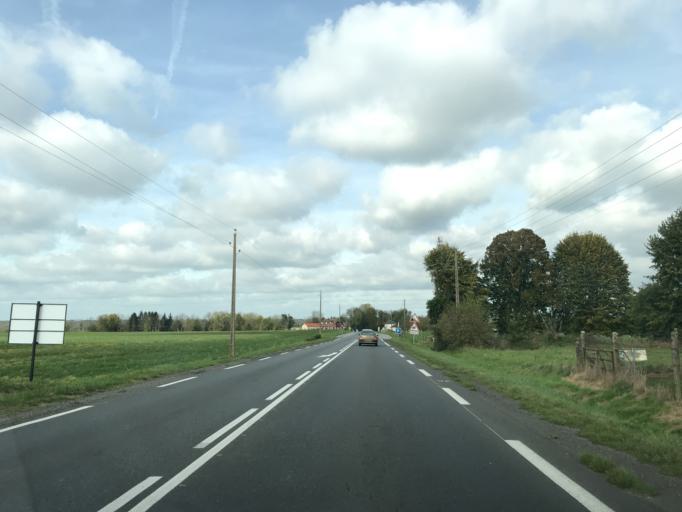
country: FR
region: Haute-Normandie
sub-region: Departement de l'Eure
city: Fleury-sur-Andelle
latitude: 49.3506
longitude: 1.3630
